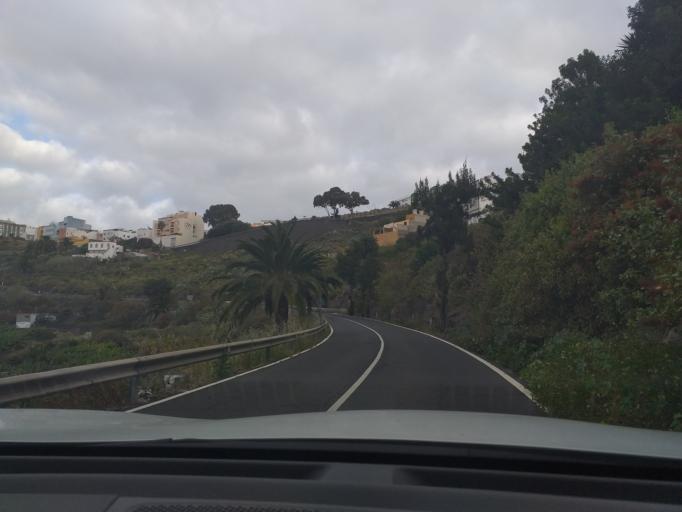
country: ES
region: Canary Islands
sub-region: Provincia de Las Palmas
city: Arucas
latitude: 28.1064
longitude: -15.5022
